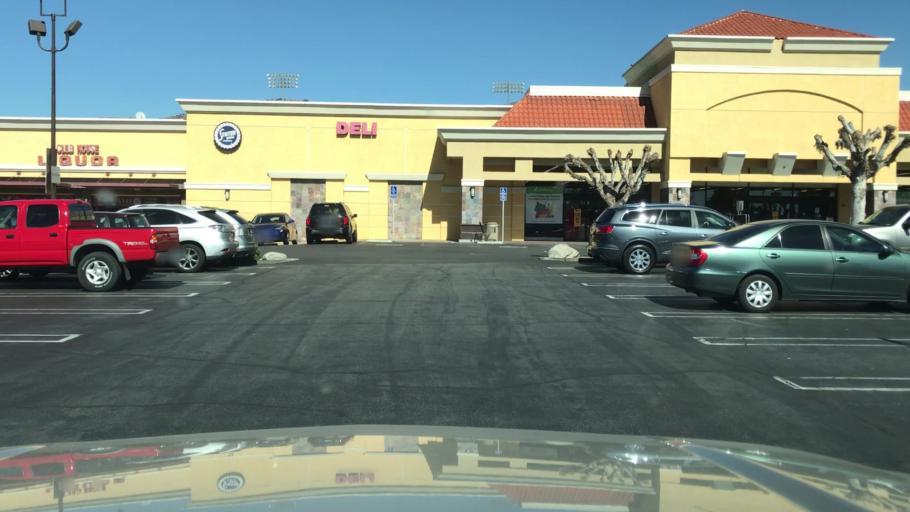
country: US
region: California
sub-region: Los Angeles County
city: Citrus
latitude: 34.1290
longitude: -117.8829
